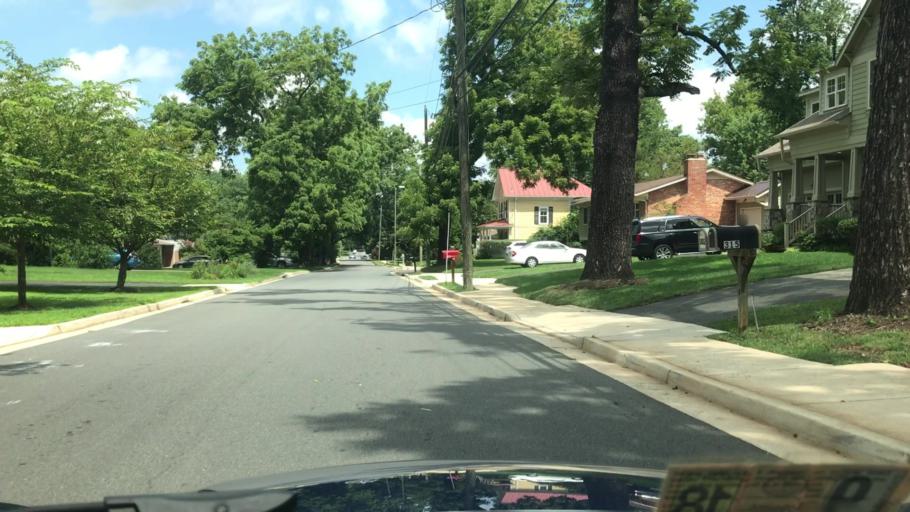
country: US
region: Virginia
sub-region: Fairfax County
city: Vienna
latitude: 38.8983
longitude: -77.2736
